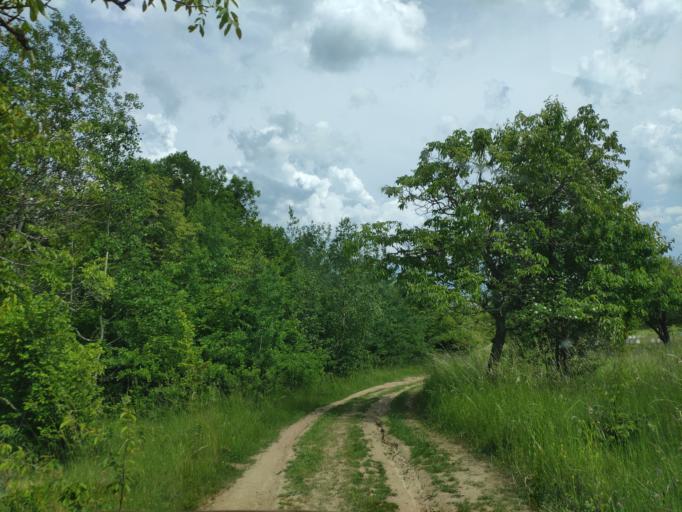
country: SK
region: Kosicky
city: Medzev
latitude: 48.7196
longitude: 20.9669
